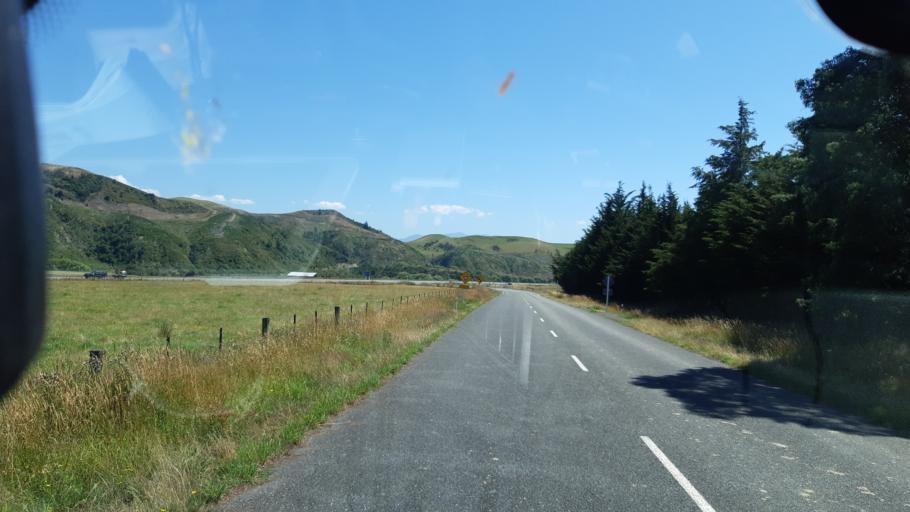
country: NZ
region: Canterbury
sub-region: Kaikoura District
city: Kaikoura
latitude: -42.6433
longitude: 173.3226
